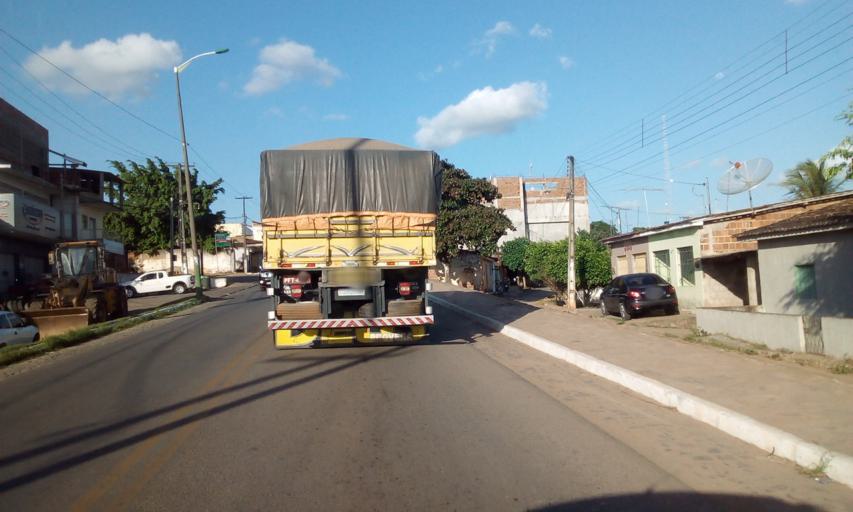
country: BR
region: Paraiba
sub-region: Mari
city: Mari
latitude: -7.1016
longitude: -35.2329
